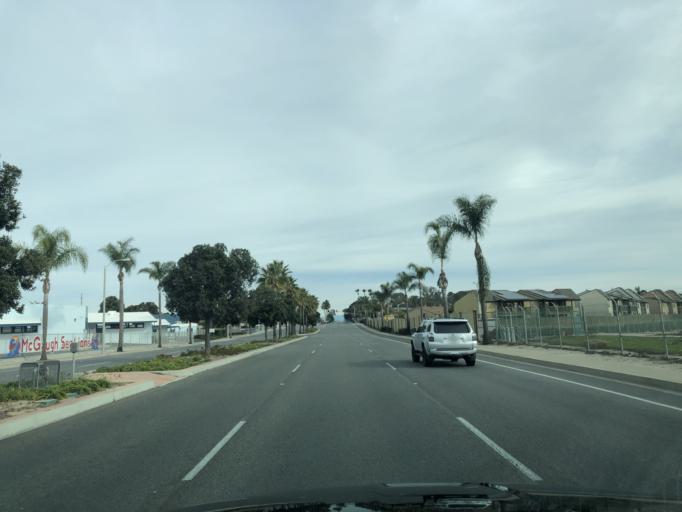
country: US
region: California
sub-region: Orange County
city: Seal Beach
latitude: 33.7427
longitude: -118.0940
